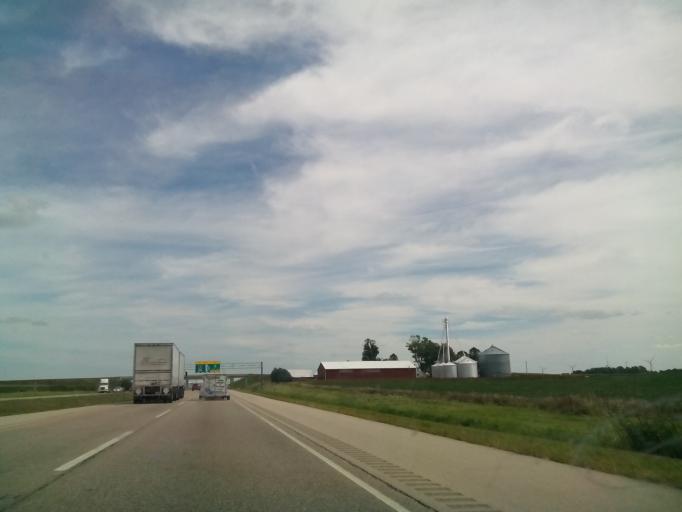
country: US
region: Illinois
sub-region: DeKalb County
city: Malta
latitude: 41.8996
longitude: -88.8906
